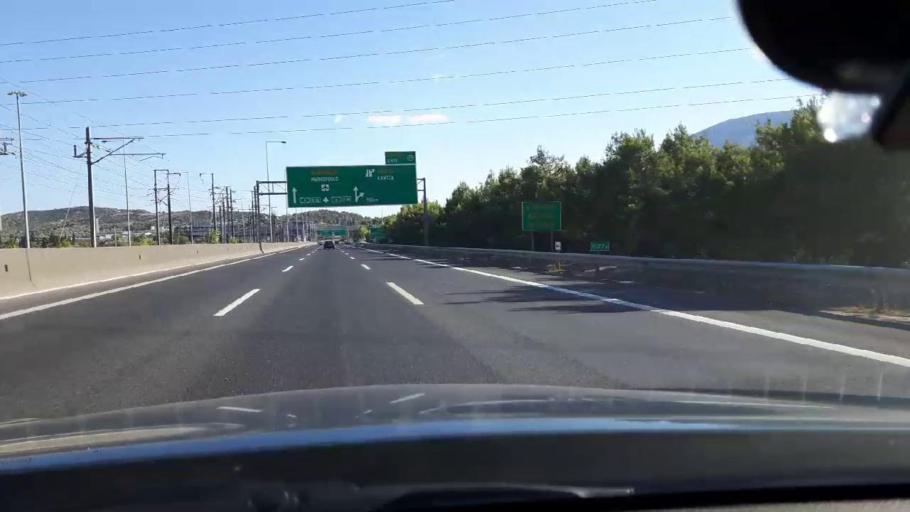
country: GR
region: Attica
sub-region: Nomarchia Anatolikis Attikis
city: Argithea
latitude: 37.9782
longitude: 23.8715
